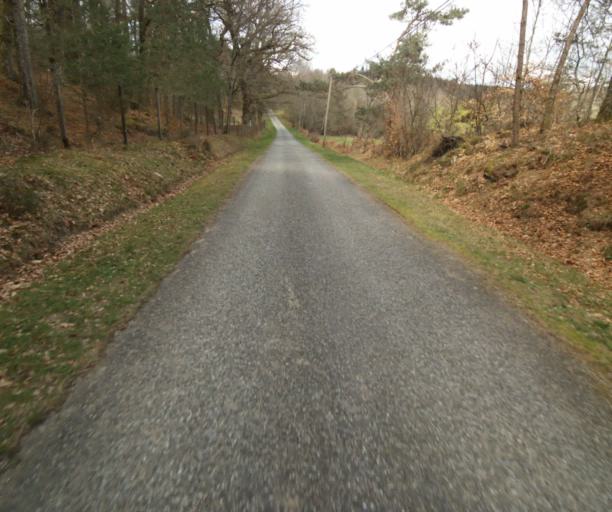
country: FR
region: Limousin
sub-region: Departement de la Correze
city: Correze
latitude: 45.2842
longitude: 1.9311
